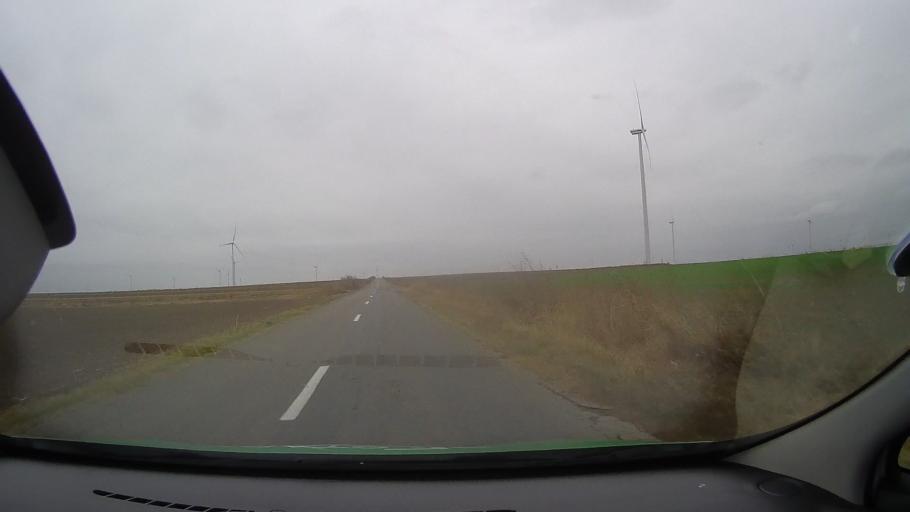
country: RO
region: Constanta
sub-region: Comuna Pantelimon
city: Pantelimon
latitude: 44.5055
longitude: 28.3468
